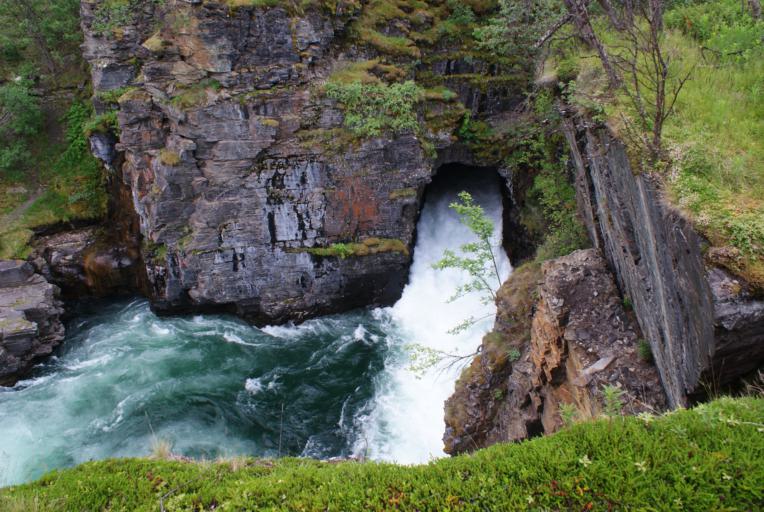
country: NO
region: Troms
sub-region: Bardu
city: Setermoen
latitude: 68.3600
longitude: 18.7756
